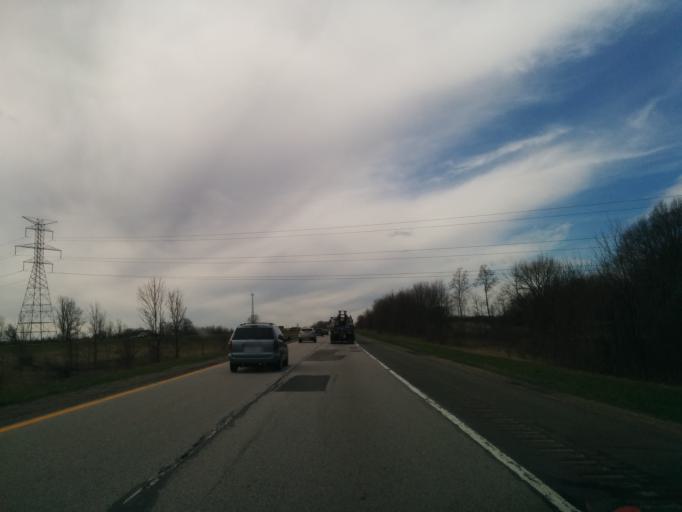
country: US
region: Michigan
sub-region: Ottawa County
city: Hudsonville
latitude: 42.8318
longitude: -85.9135
